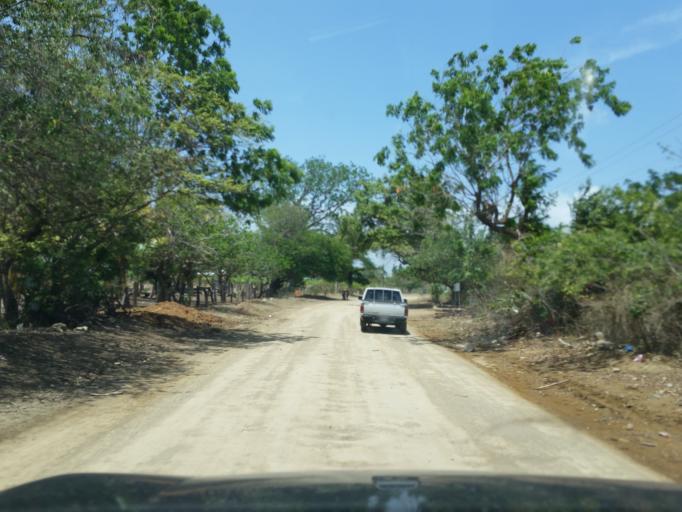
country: NI
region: Rivas
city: Tola
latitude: 11.4515
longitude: -86.0651
